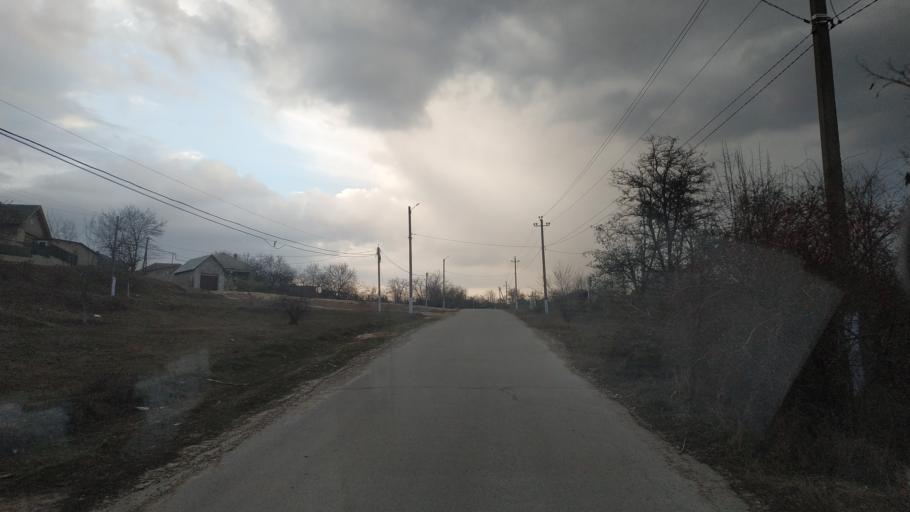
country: MD
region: Telenesti
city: Grigoriopol
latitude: 47.0242
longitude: 29.3577
